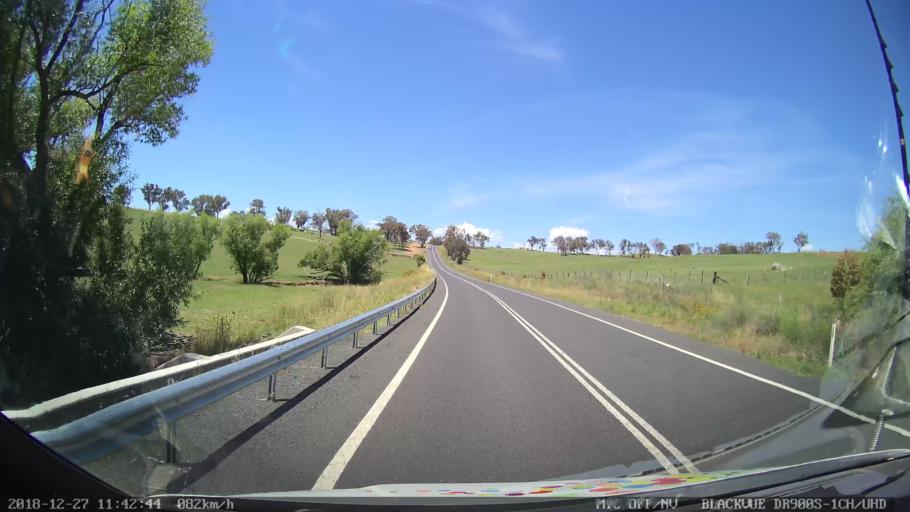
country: AU
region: New South Wales
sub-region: Bathurst Regional
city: Perthville
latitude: -33.5520
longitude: 149.4775
